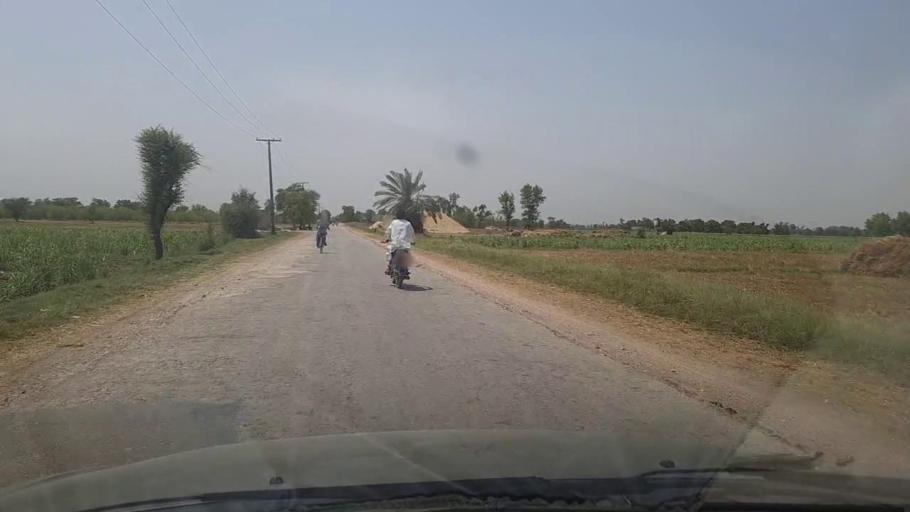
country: PK
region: Sindh
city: Bhiria
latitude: 26.8944
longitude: 68.2419
